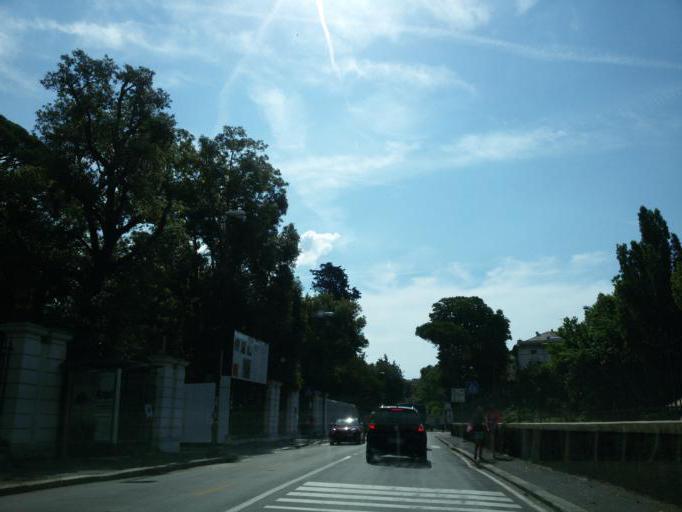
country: IT
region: Liguria
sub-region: Provincia di Genova
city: Genoa
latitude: 44.3962
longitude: 8.9725
